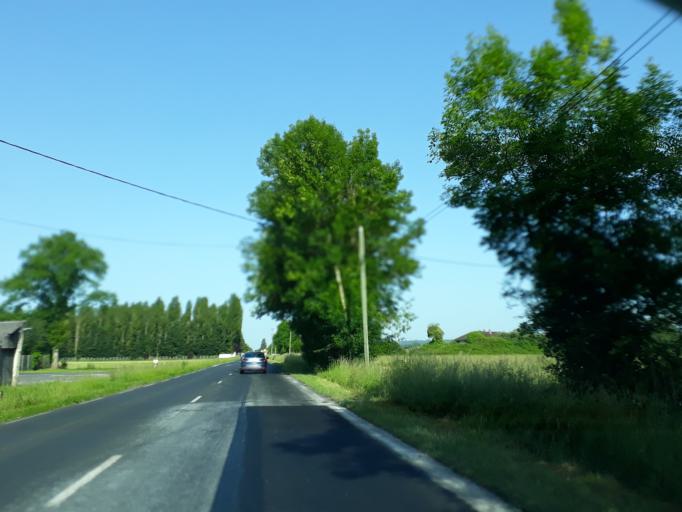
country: FR
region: Limousin
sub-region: Departement de la Correze
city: Larche
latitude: 45.1256
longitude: 1.3914
